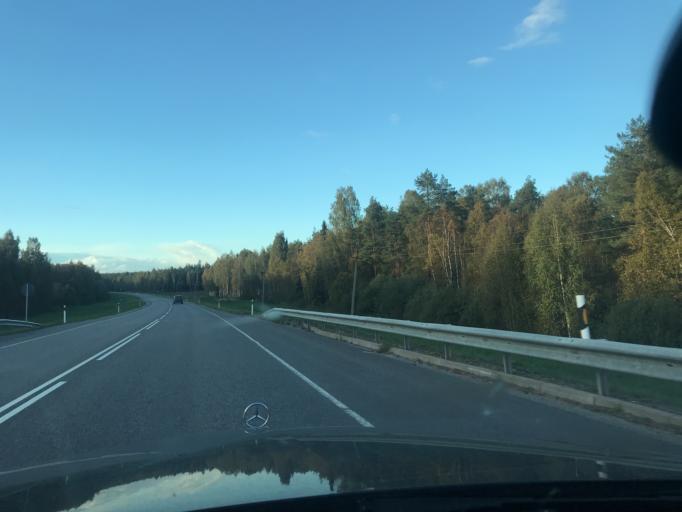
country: EE
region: Vorumaa
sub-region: Voru linn
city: Voru
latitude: 57.8293
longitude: 27.0630
